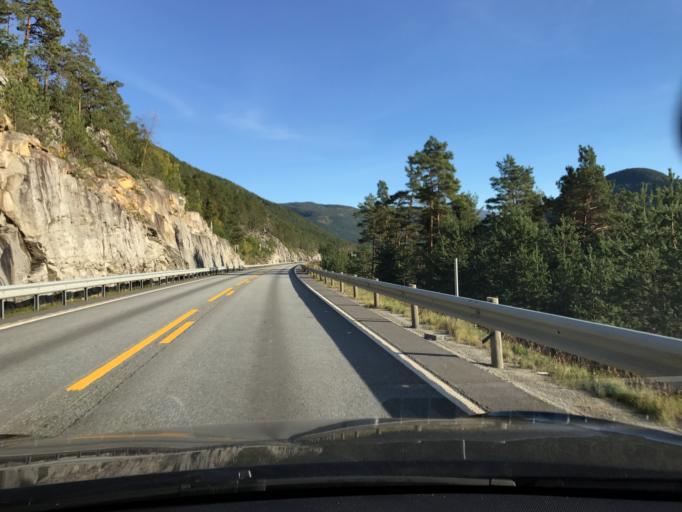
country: NO
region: Sogn og Fjordane
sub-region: Sogndal
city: Sogndalsfjora
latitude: 61.1882
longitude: 7.2372
